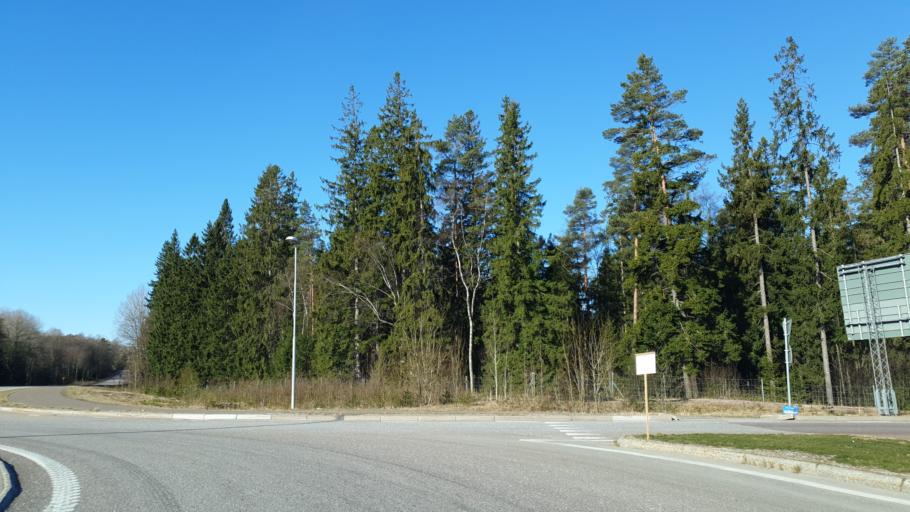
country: SE
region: Vaestra Goetaland
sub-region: Boras Kommun
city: Dalsjofors
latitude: 57.7571
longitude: 13.1043
